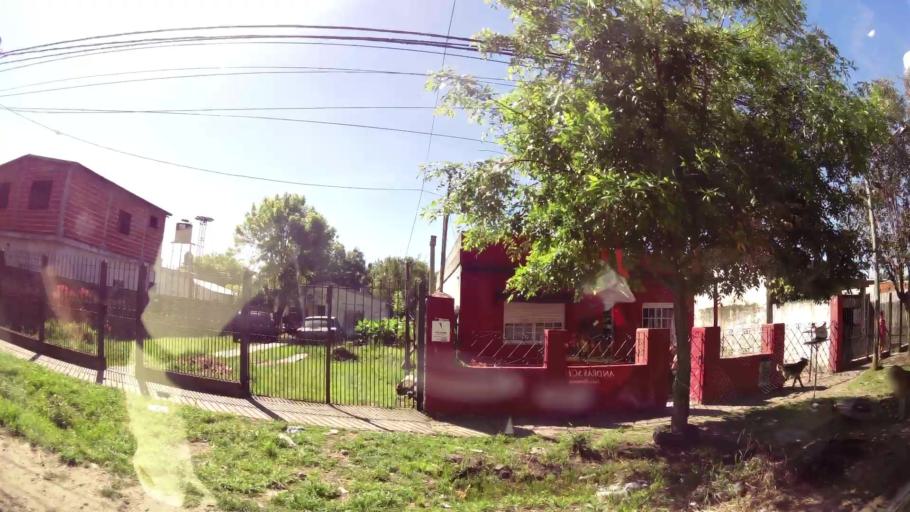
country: AR
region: Buenos Aires
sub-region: Partido de Almirante Brown
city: Adrogue
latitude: -34.7843
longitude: -58.3493
